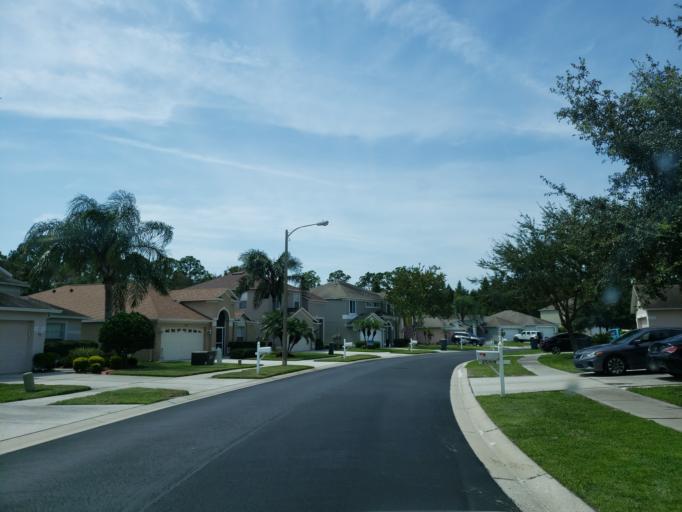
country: US
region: Florida
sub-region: Pasco County
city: Land O' Lakes
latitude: 28.2263
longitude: -82.3933
